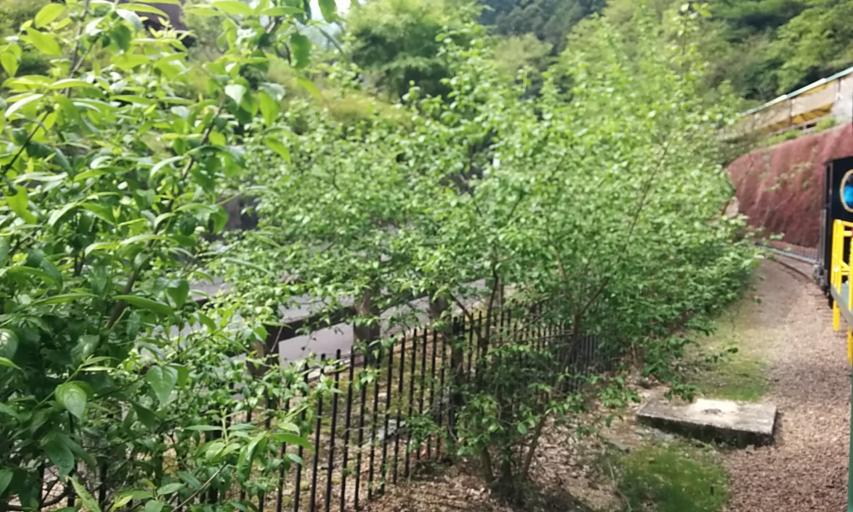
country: JP
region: Ehime
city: Niihama
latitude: 33.9016
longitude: 133.3091
